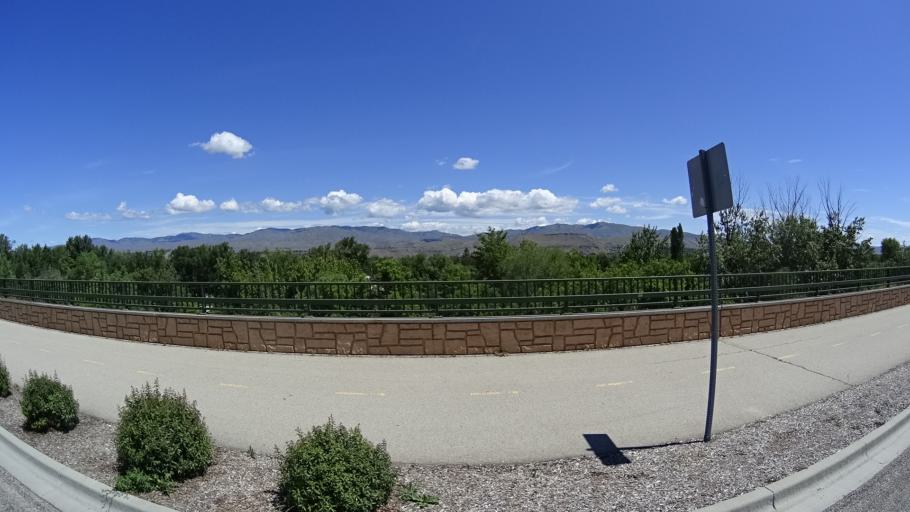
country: US
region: Idaho
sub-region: Ada County
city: Boise
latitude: 43.5826
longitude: -116.1993
